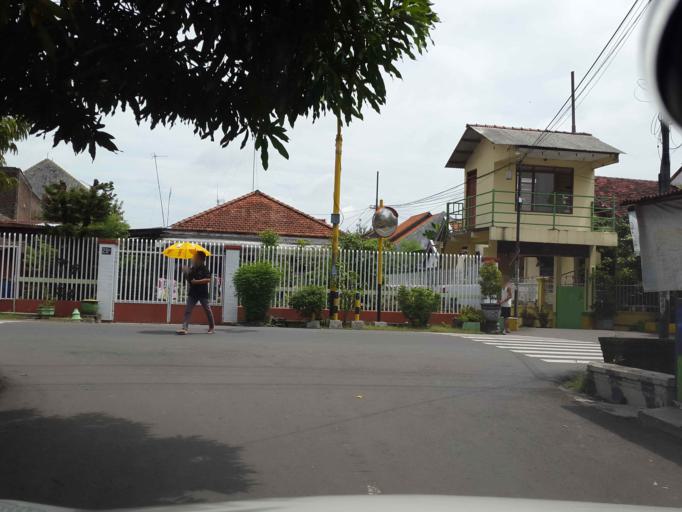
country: ID
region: East Java
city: Mojokerto
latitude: -7.4572
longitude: 112.4467
